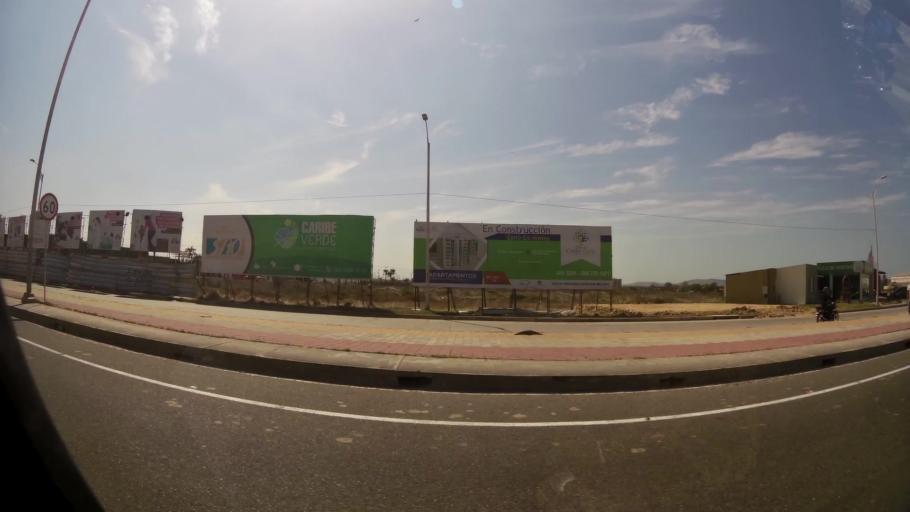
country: CO
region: Atlantico
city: Barranquilla
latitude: 10.9579
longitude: -74.8368
